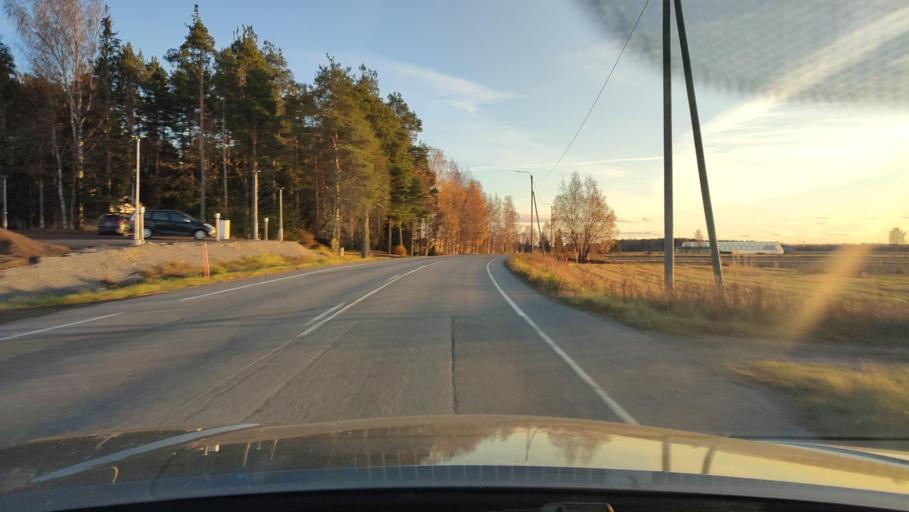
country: FI
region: Ostrobothnia
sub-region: Sydosterbotten
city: Naerpes
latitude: 62.4459
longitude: 21.3515
